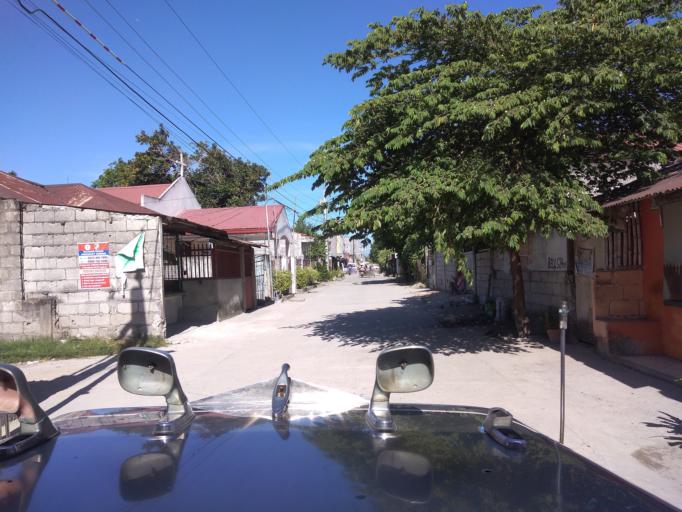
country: PH
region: Central Luzon
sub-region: Province of Pampanga
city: Calibutbut
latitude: 15.0996
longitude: 120.6059
